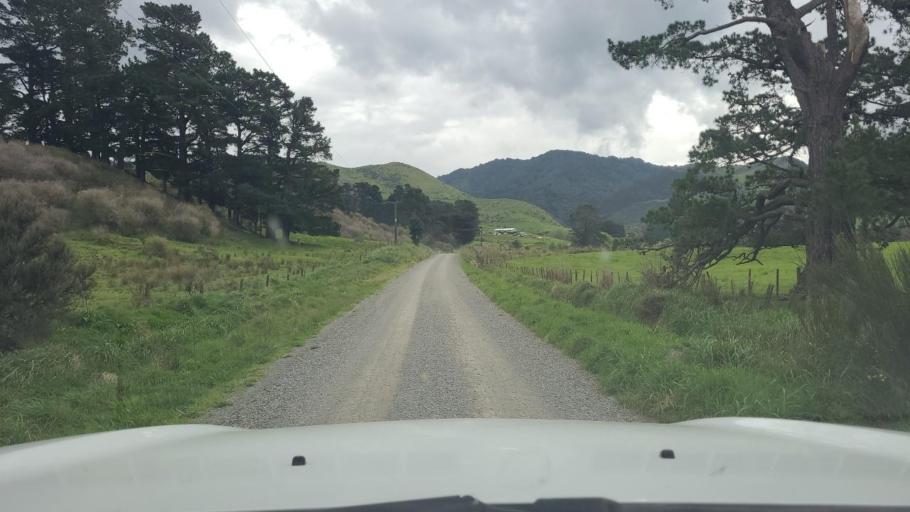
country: NZ
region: Wellington
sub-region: Masterton District
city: Masterton
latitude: -40.9733
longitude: 175.4956
